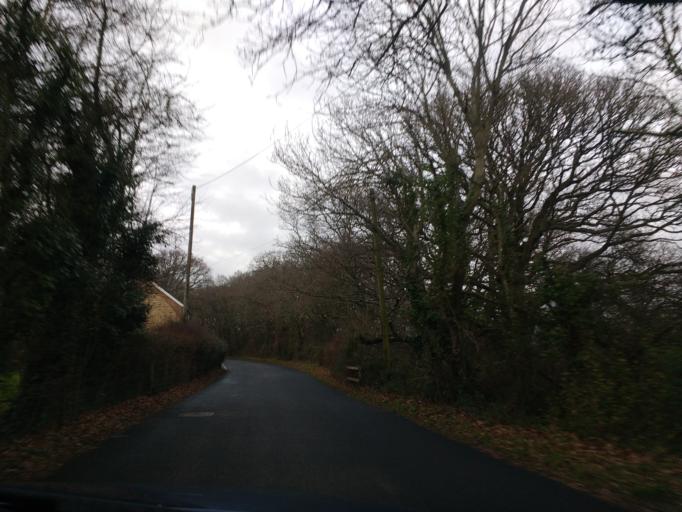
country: GB
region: England
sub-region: Isle of Wight
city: Shalfleet
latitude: 50.7134
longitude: -1.3728
